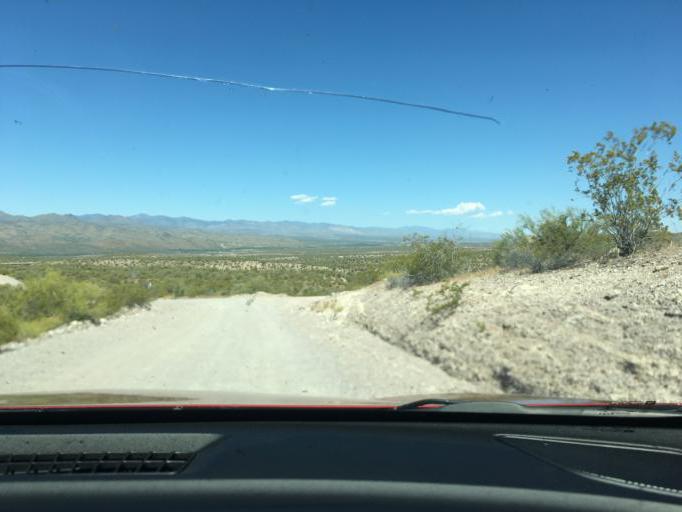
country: US
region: Arizona
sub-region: Yavapai County
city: Bagdad
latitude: 34.6099
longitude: -113.5121
